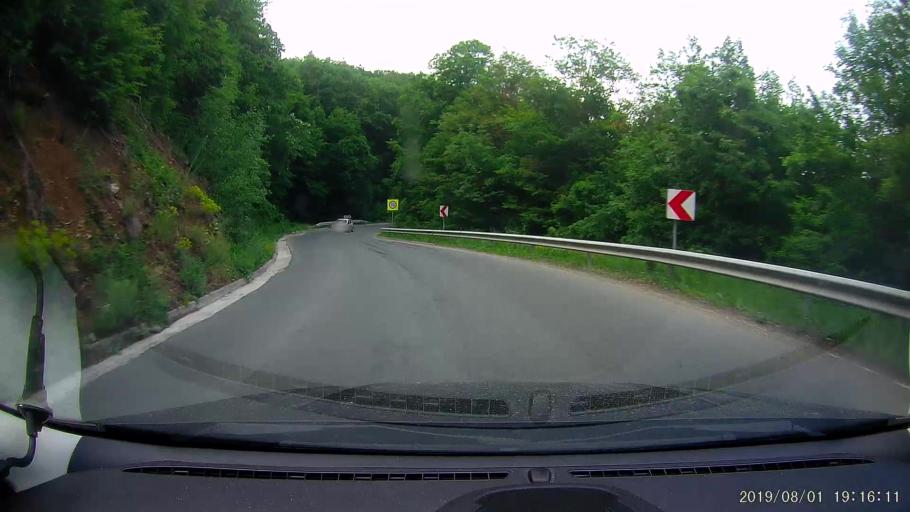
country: BG
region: Shumen
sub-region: Obshtina Smyadovo
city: Smyadovo
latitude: 42.9308
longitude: 26.9484
